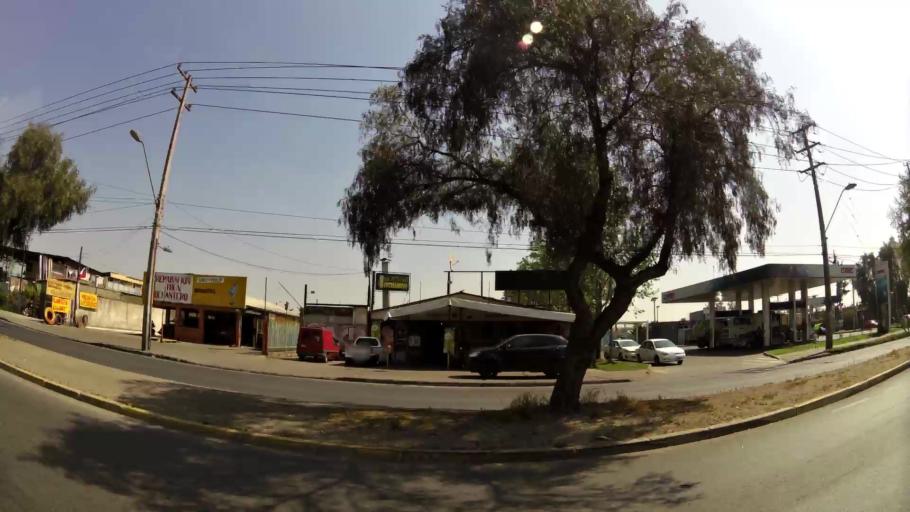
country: CL
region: Santiago Metropolitan
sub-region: Provincia de Santiago
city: La Pintana
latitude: -33.5473
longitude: -70.6034
